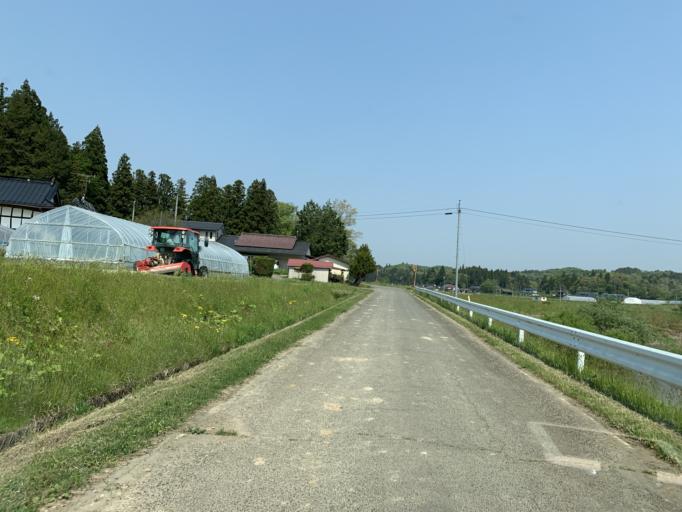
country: JP
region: Iwate
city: Ichinoseki
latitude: 38.8560
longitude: 141.0725
